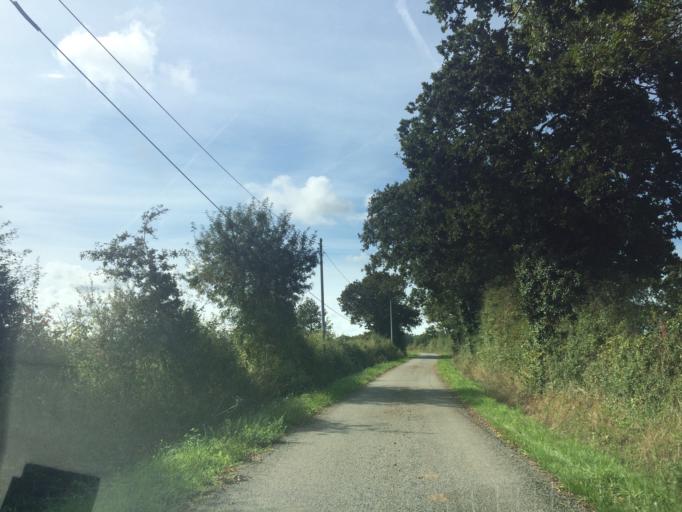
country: FR
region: Pays de la Loire
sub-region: Departement de la Loire-Atlantique
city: Chemere
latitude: 47.1224
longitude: -1.8899
